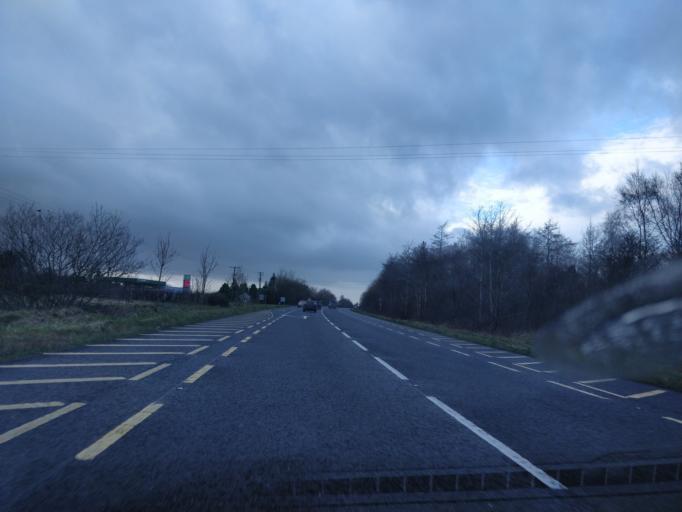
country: IE
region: Connaught
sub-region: Maigh Eo
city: Swinford
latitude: 53.9267
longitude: -8.9610
